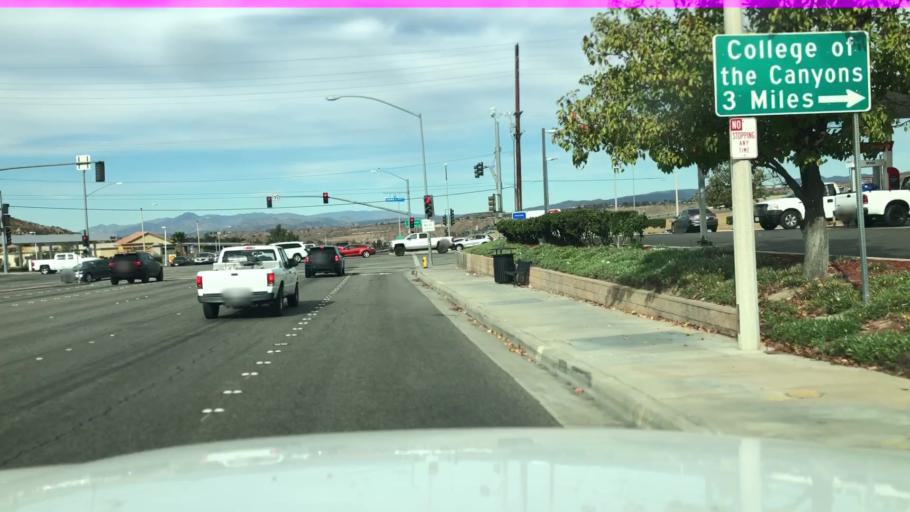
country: US
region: California
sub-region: Los Angeles County
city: Santa Clarita
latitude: 34.4052
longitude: -118.4641
